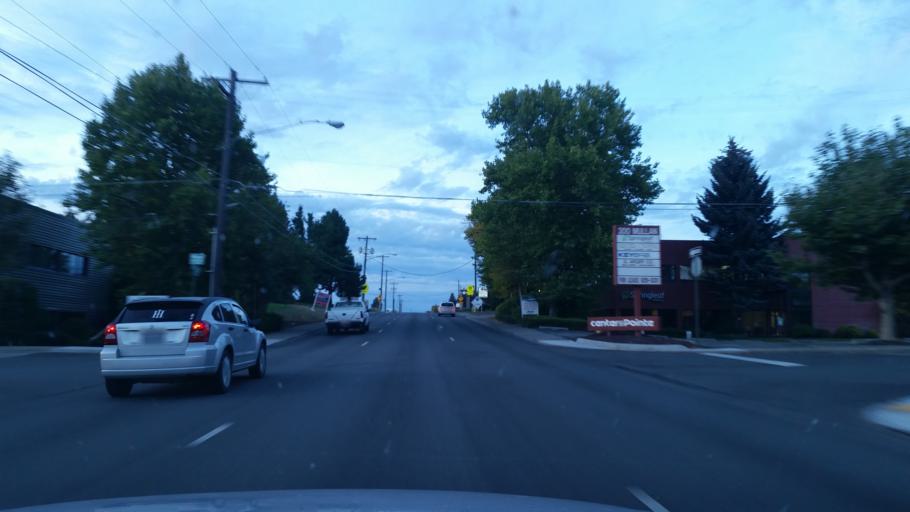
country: US
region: Washington
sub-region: Spokane County
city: Dishman
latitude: 47.6591
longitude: -117.2815
